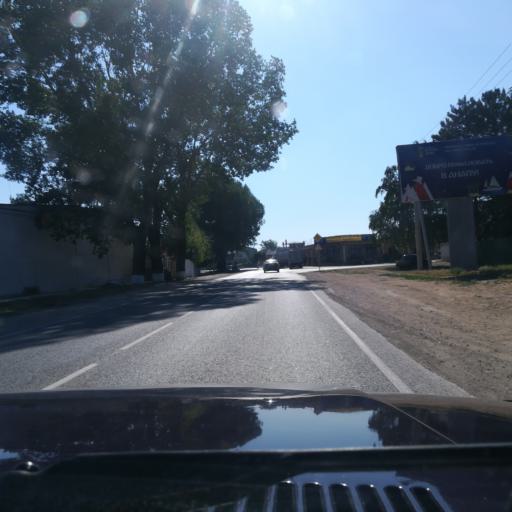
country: RU
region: Krasnodarskiy
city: Vityazevo
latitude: 45.0020
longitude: 37.2890
